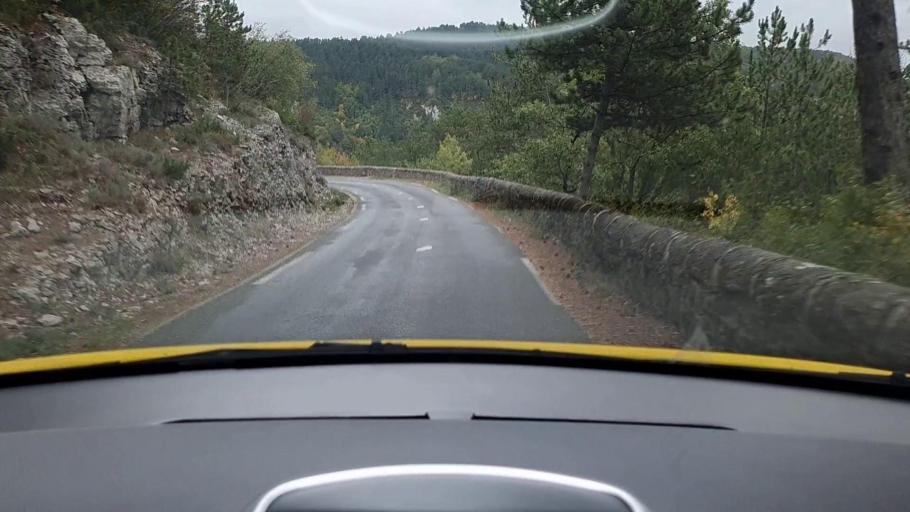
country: FR
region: Languedoc-Roussillon
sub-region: Departement de la Lozere
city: Meyrueis
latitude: 44.0797
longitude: 3.3599
